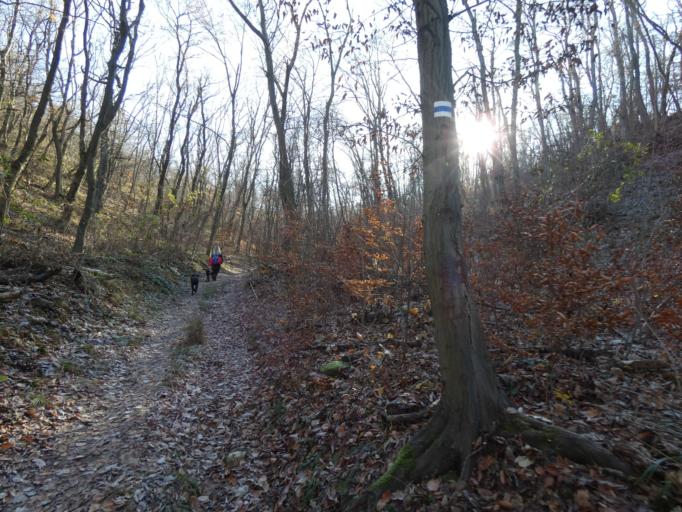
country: HU
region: Pest
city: Pilisszentivan
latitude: 47.5937
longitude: 18.8556
